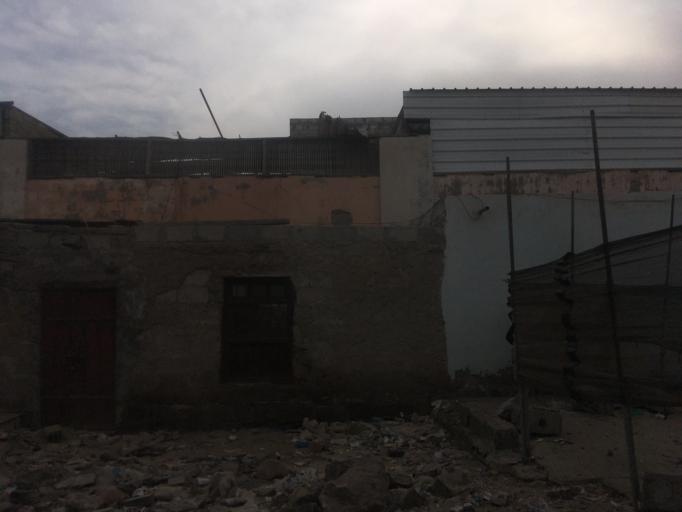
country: YE
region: Aden
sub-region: Al Mansura
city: Al Mansurah
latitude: 12.8566
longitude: 44.9905
